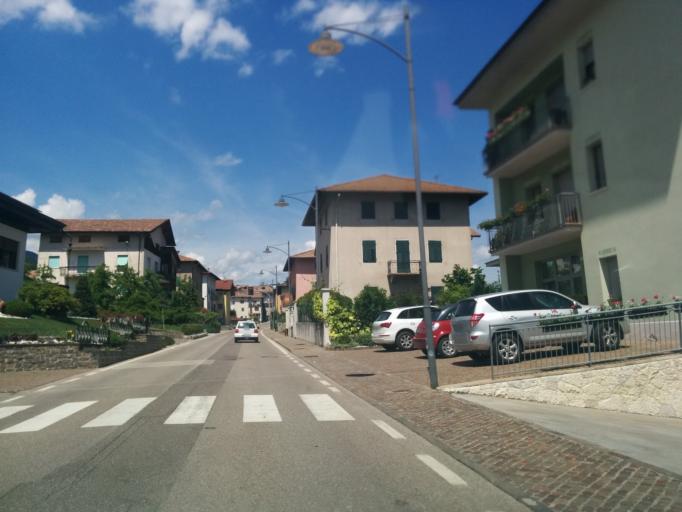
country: IT
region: Trentino-Alto Adige
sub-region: Provincia di Trento
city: Tuenno
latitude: 46.3235
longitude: 11.0220
